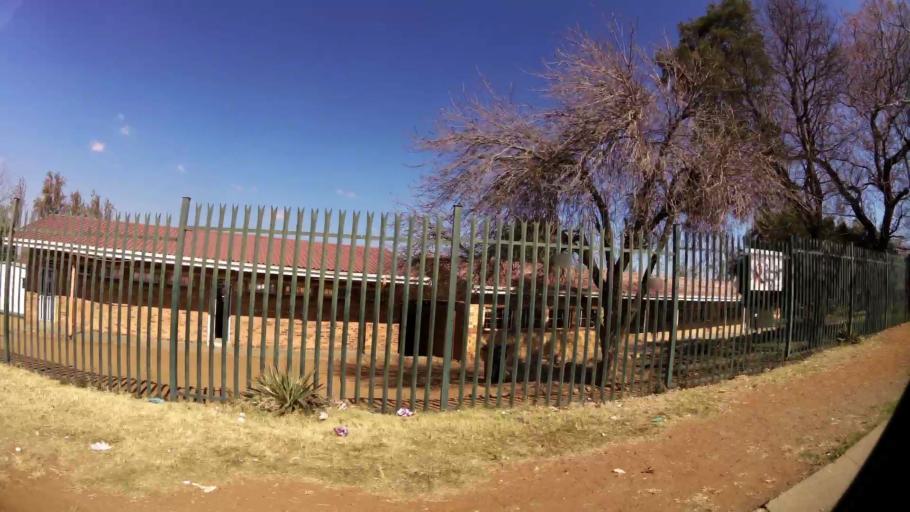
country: ZA
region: Gauteng
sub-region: City of Johannesburg Metropolitan Municipality
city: Soweto
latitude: -26.2422
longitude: 27.9031
